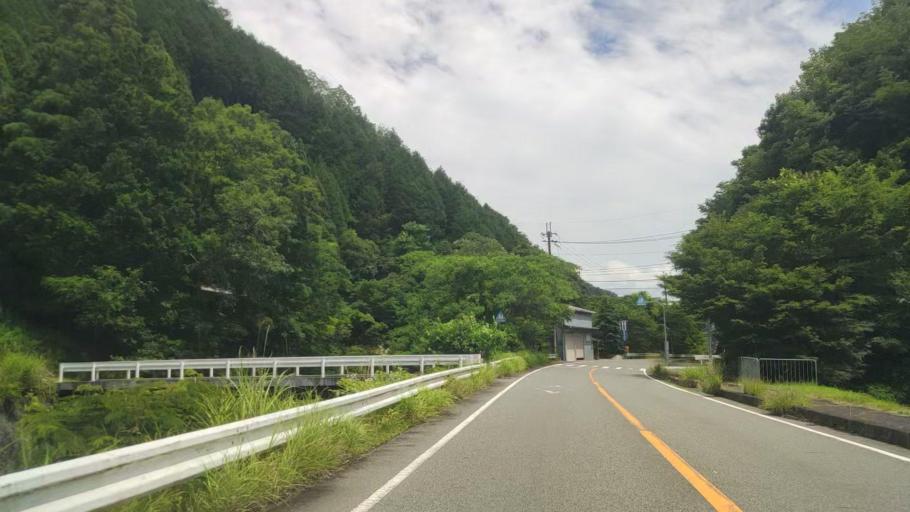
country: JP
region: Hyogo
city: Yamazakicho-nakabirose
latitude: 35.0667
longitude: 134.3618
